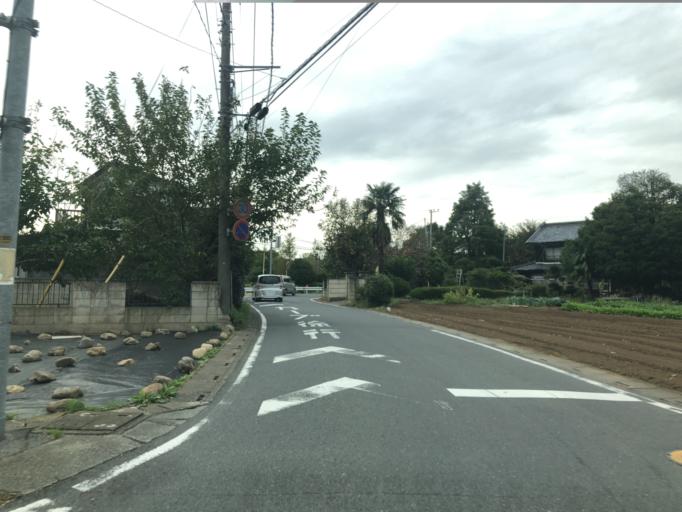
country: JP
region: Saitama
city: Fukiage-fujimi
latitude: 36.0526
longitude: 139.4038
